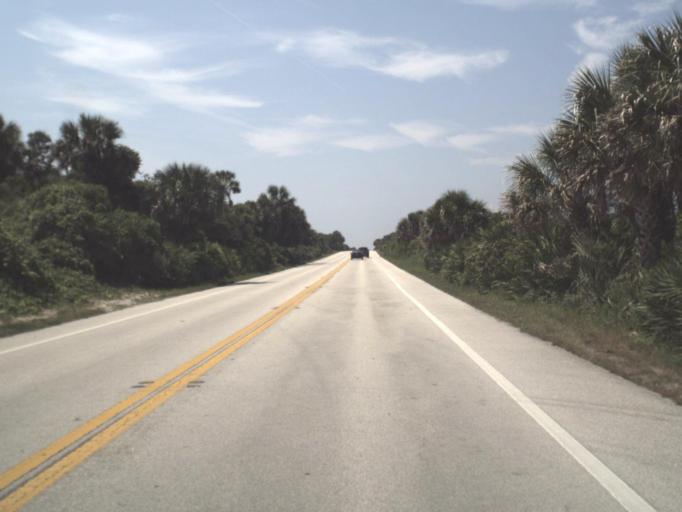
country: US
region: Florida
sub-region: Saint Johns County
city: Palm Valley
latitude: 30.1268
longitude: -81.3483
